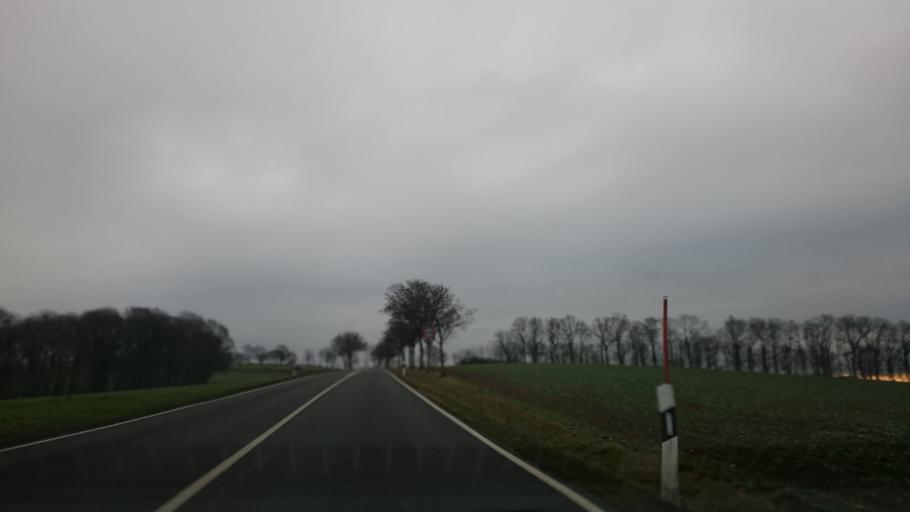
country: DE
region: Saxony
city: Mulsen
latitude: 50.7428
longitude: 12.5783
